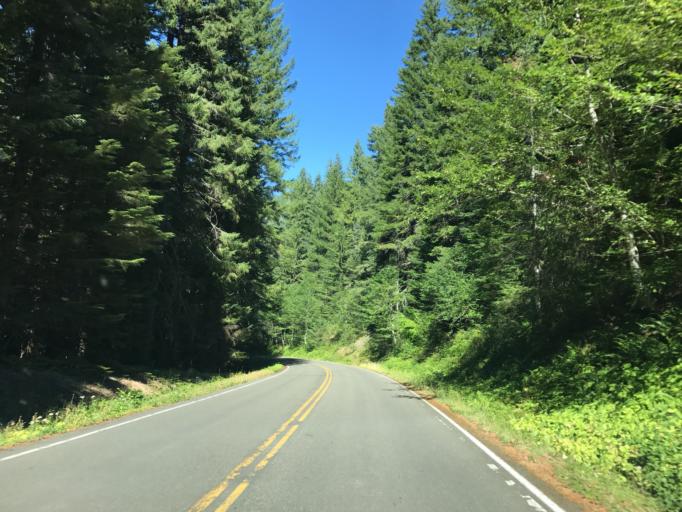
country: US
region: Washington
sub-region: Pierce County
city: Buckley
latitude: 46.7364
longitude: -121.6136
